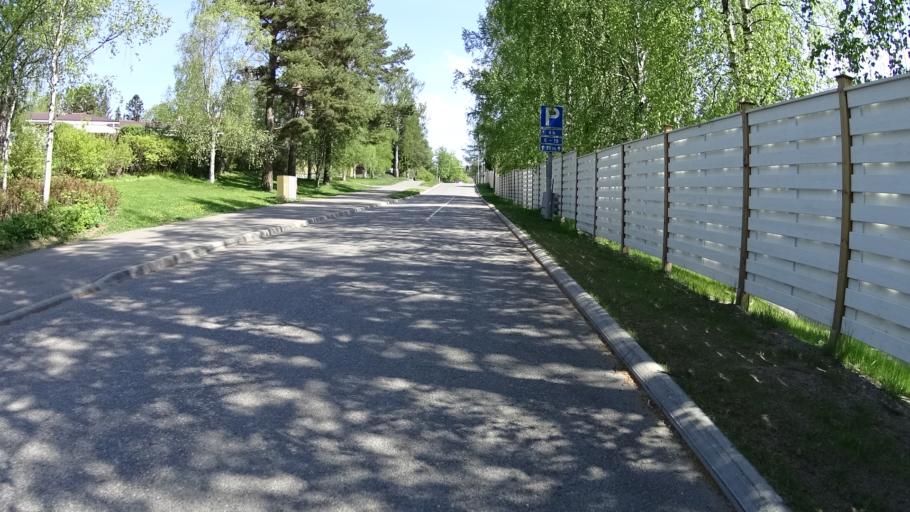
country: FI
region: Uusimaa
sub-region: Helsinki
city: Kilo
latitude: 60.1879
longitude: 24.7716
